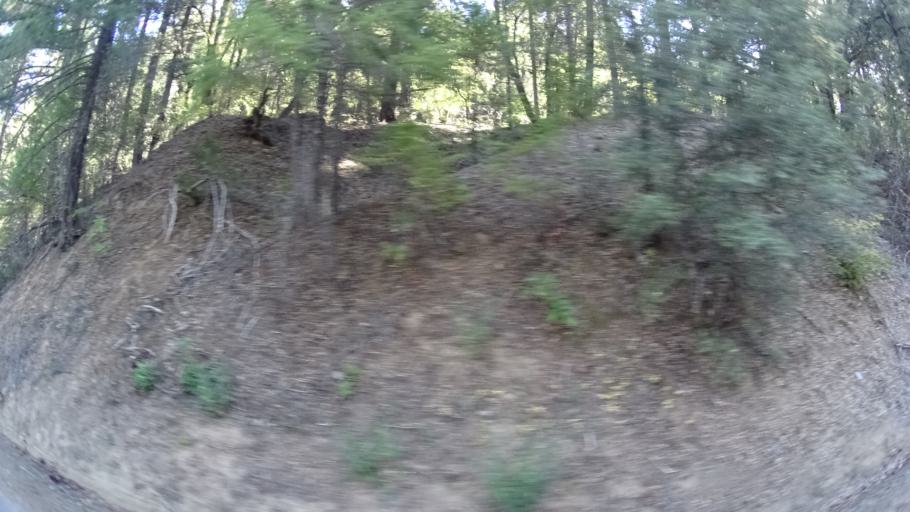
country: US
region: California
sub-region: Humboldt County
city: Willow Creek
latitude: 41.1912
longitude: -123.2159
